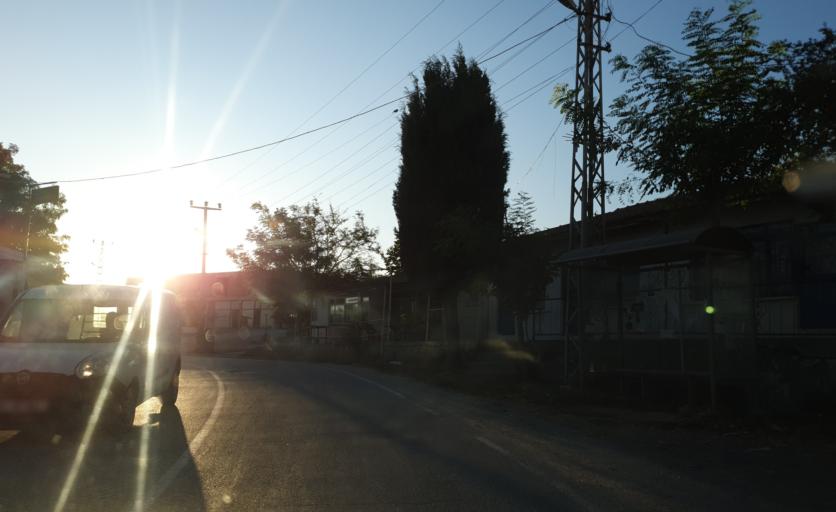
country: TR
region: Tekirdag
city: Beyazkoy
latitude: 41.3362
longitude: 27.7364
